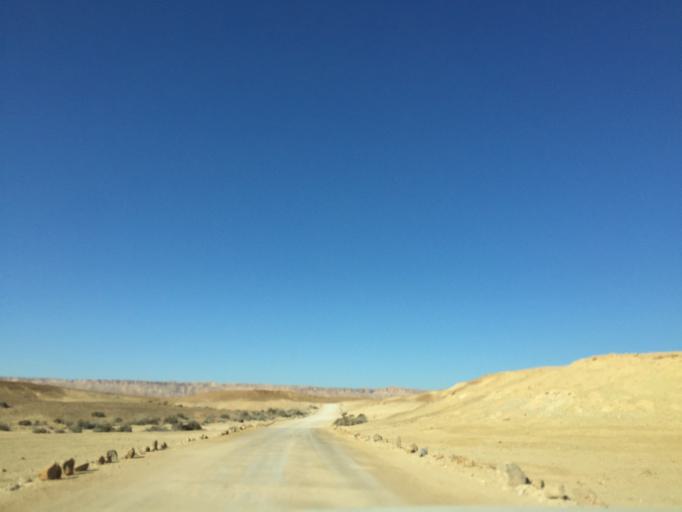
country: IL
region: Southern District
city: Mitzpe Ramon
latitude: 30.6155
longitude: 34.9317
